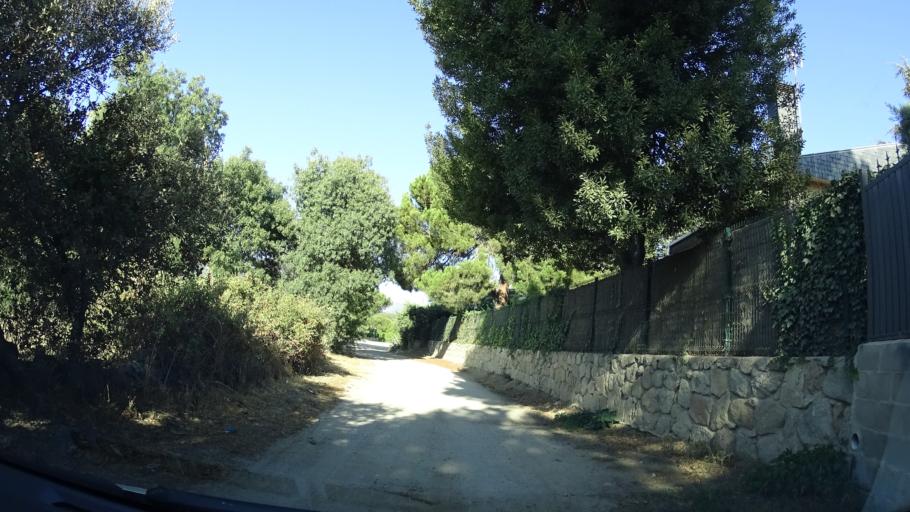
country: ES
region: Madrid
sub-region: Provincia de Madrid
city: Colmenarejo
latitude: 40.5581
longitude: -4.0215
